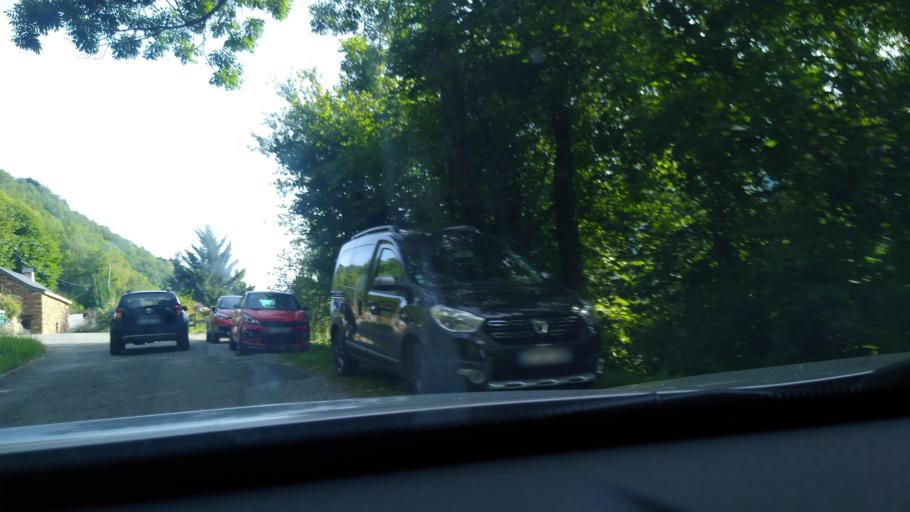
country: FR
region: Midi-Pyrenees
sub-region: Departement de l'Ariege
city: Saint-Girons
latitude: 42.7971
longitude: 1.1871
